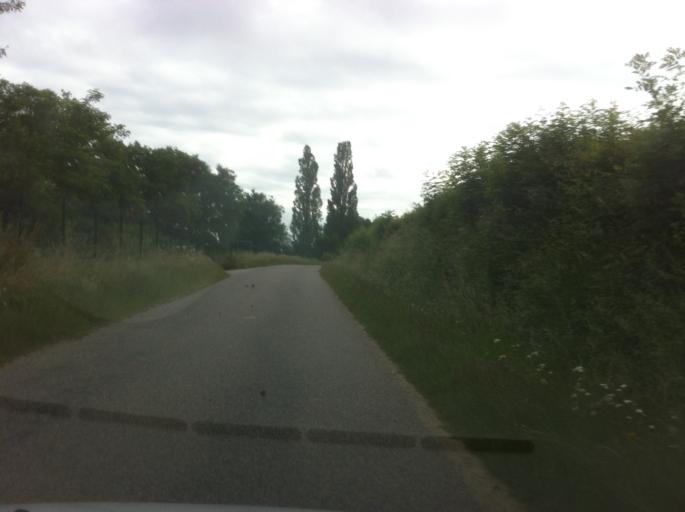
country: FR
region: Auvergne
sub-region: Departement de l'Allier
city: Montmarault
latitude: 46.3299
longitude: 3.0736
